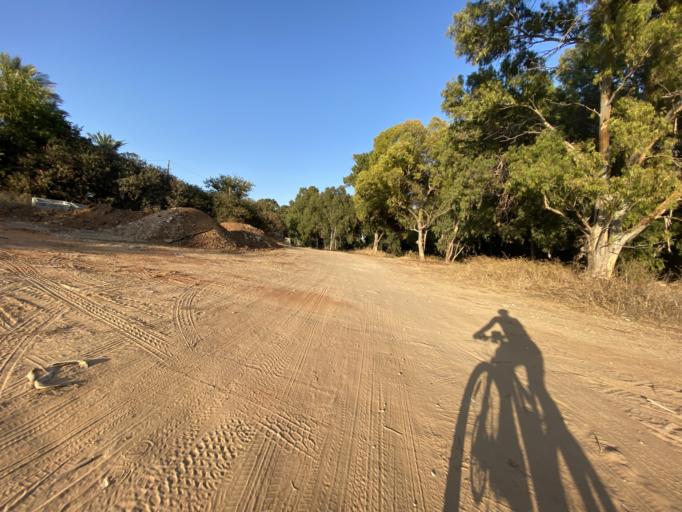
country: IL
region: Tel Aviv
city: Ramat HaSharon
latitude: 32.1562
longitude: 34.8328
